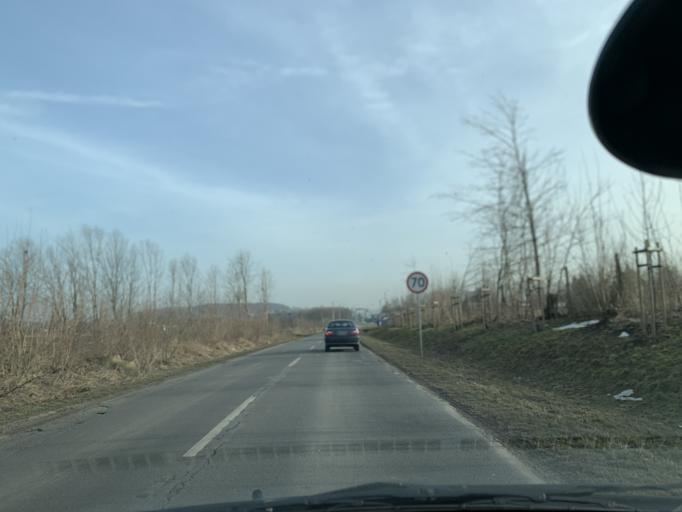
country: PL
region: Silesian Voivodeship
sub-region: Powiat tarnogorski
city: Radzionkow
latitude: 50.4103
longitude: 18.8945
